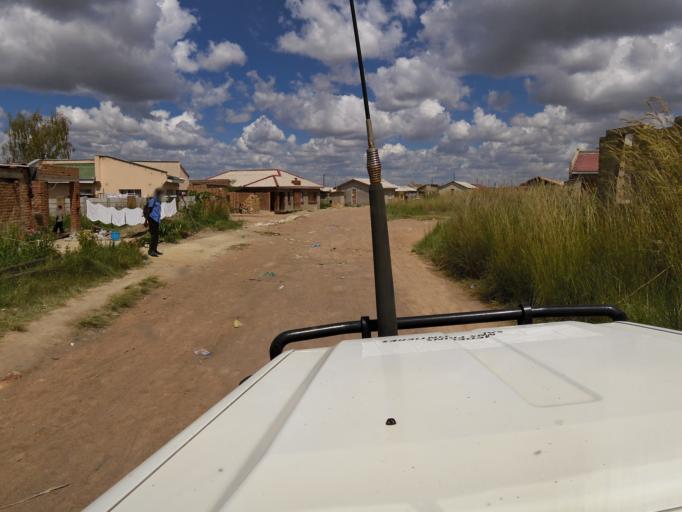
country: ZW
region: Harare
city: Epworth
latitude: -17.9189
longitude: 31.1425
